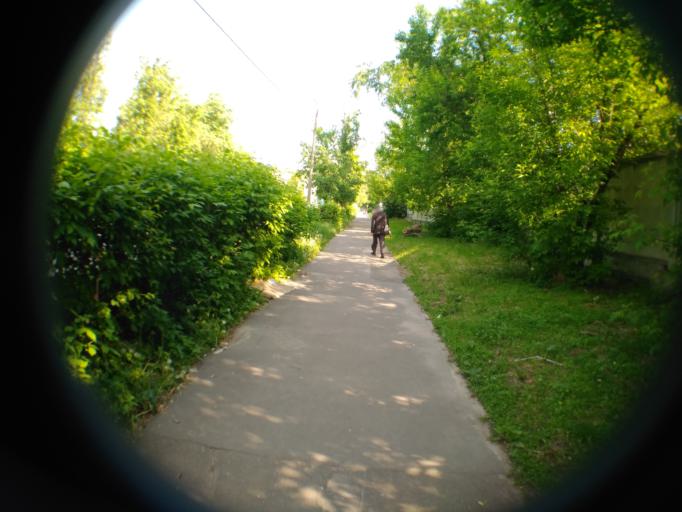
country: RU
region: Moskovskaya
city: Zhukovskiy
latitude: 55.6020
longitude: 38.1204
